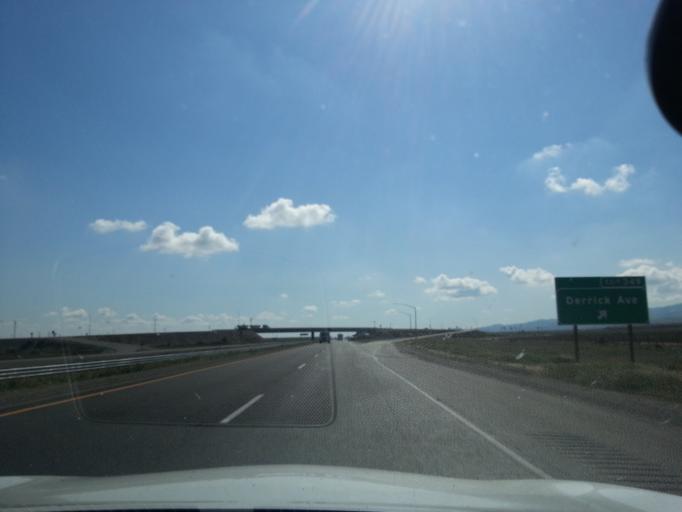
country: US
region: California
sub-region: Fresno County
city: San Joaquin
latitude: 36.4383
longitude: -120.3968
